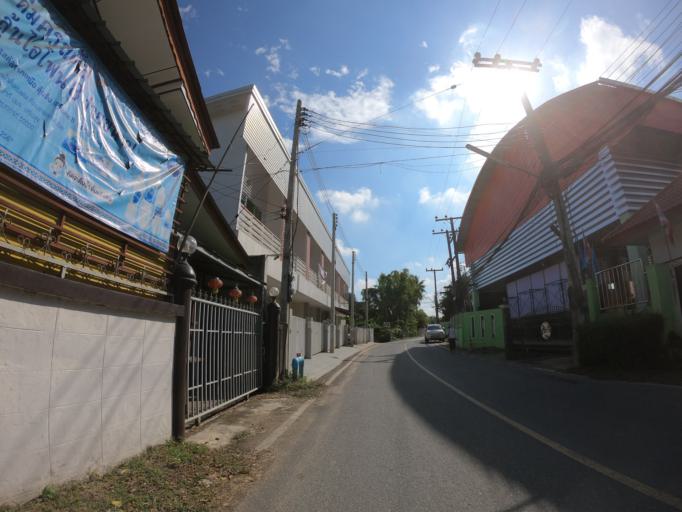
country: TH
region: Chiang Mai
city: San Sai
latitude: 18.8376
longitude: 99.0578
